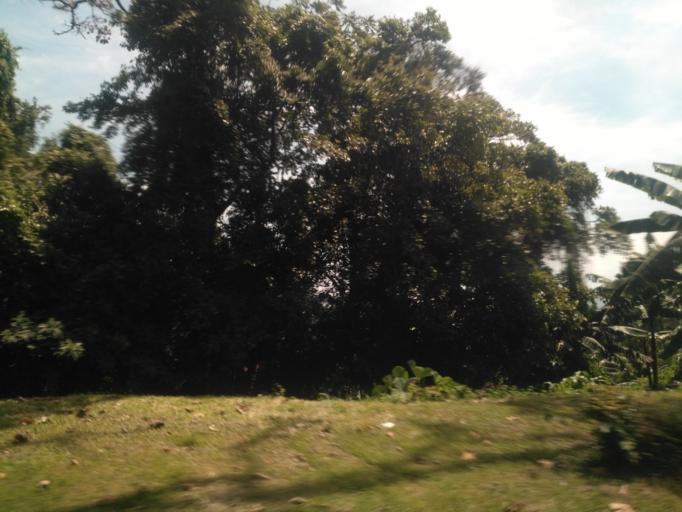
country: UG
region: Central Region
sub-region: Wakiso District
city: Entebbe
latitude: 0.0432
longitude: 32.4642
